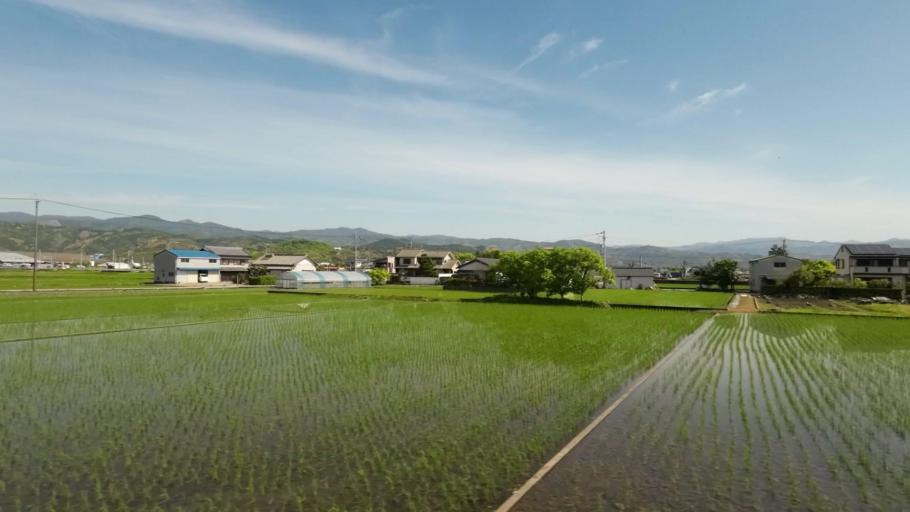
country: JP
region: Kochi
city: Kochi-shi
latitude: 33.5783
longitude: 133.6287
